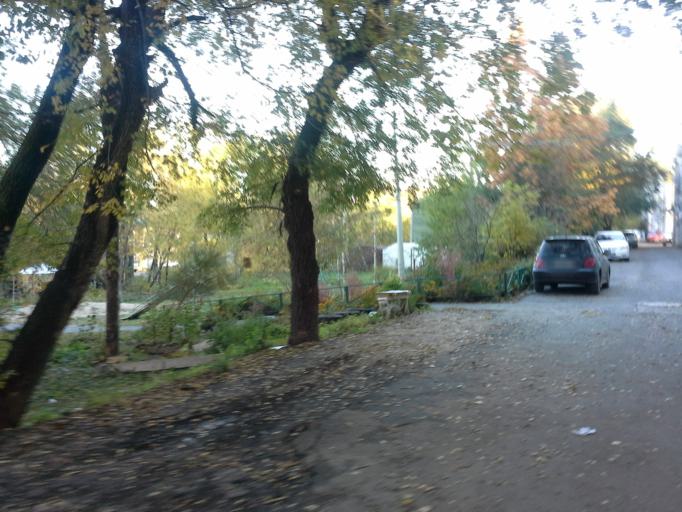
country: RU
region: Khabarovsk Krai
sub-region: Khabarovskiy Rayon
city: Khabarovsk
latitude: 48.4870
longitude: 135.0628
